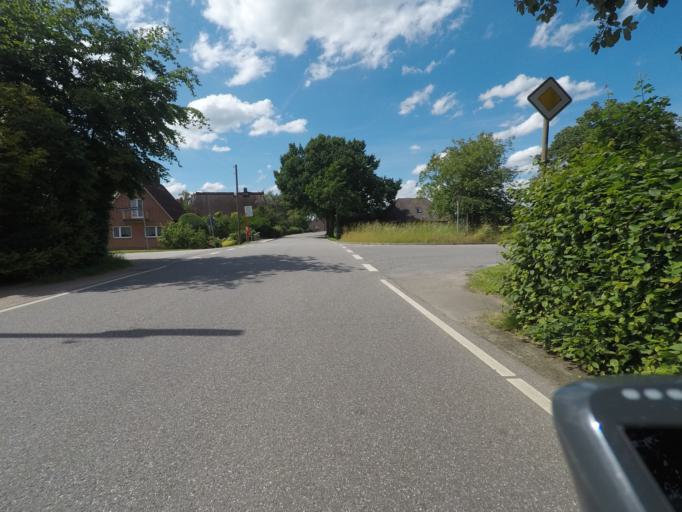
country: DE
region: Lower Saxony
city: Drage
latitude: 53.4240
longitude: 10.2537
